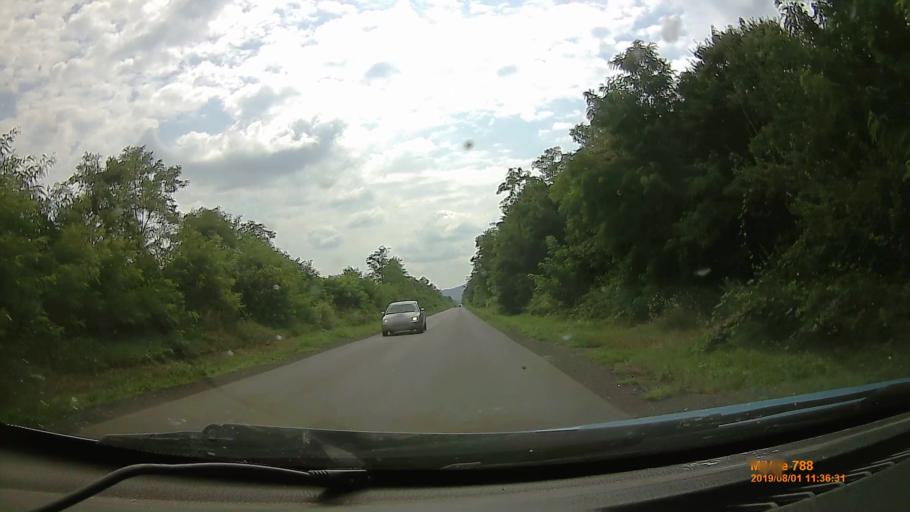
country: HU
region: Baranya
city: Villany
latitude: 45.9163
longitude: 18.3760
